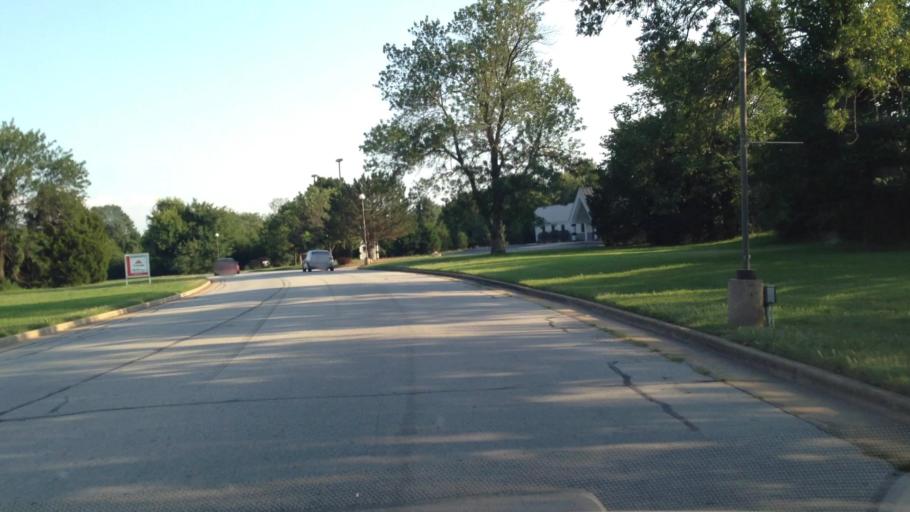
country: US
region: Missouri
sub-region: Jasper County
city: Duquesne
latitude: 37.0544
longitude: -94.4751
